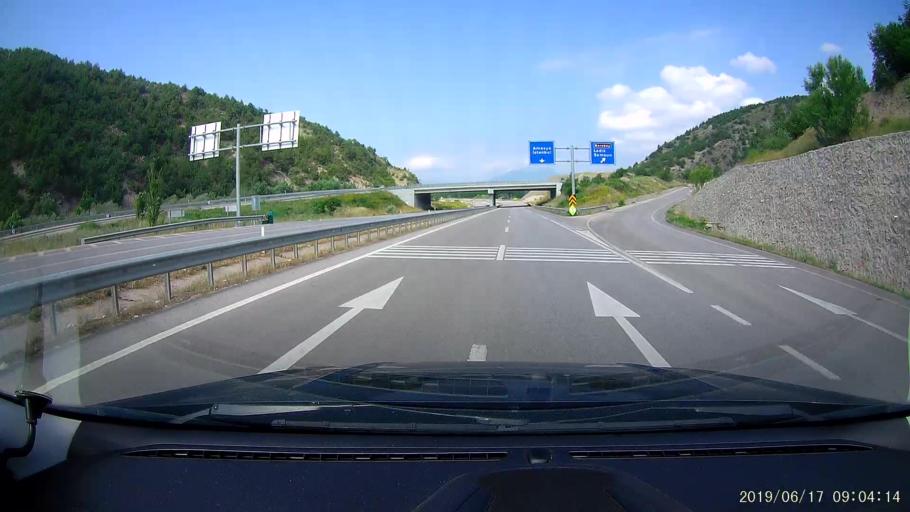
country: TR
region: Amasya
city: Tasova
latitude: 40.7468
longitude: 36.2926
